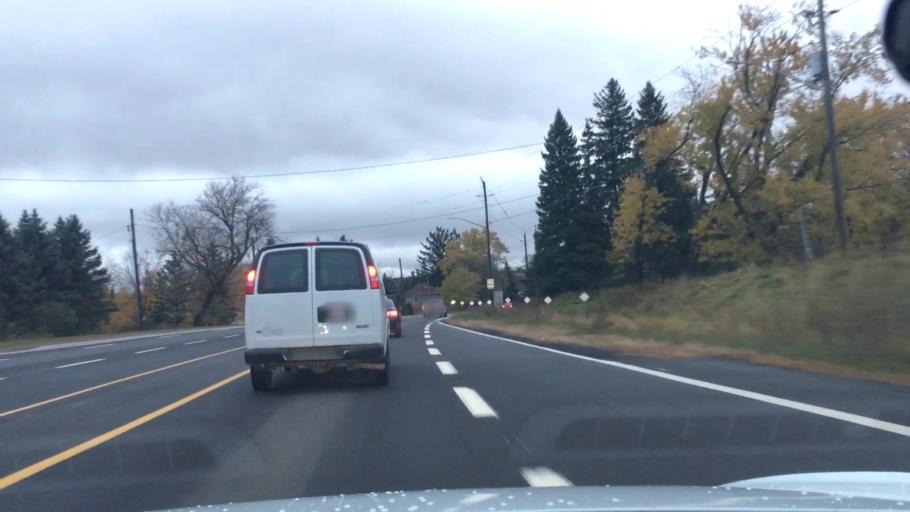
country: CA
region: Ontario
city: Pickering
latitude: 43.8999
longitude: -79.1882
